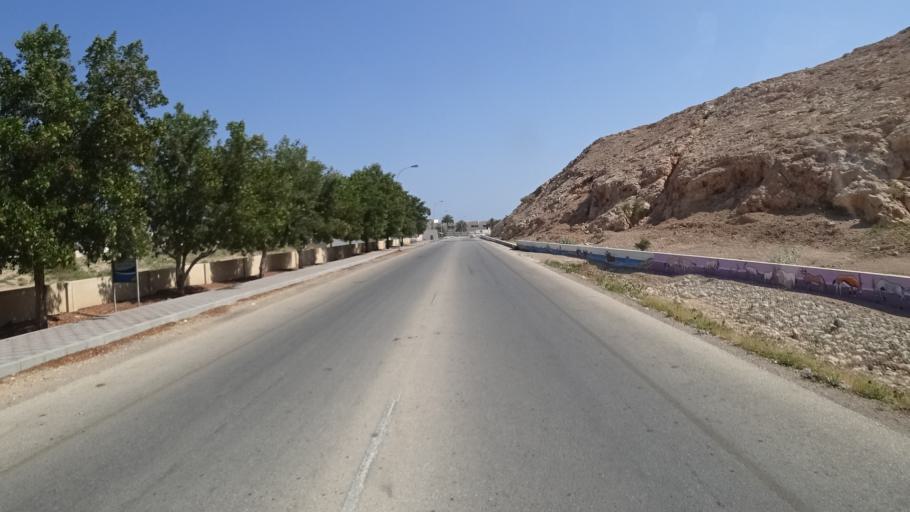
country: OM
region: Ash Sharqiyah
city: Sur
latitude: 22.5638
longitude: 59.5472
